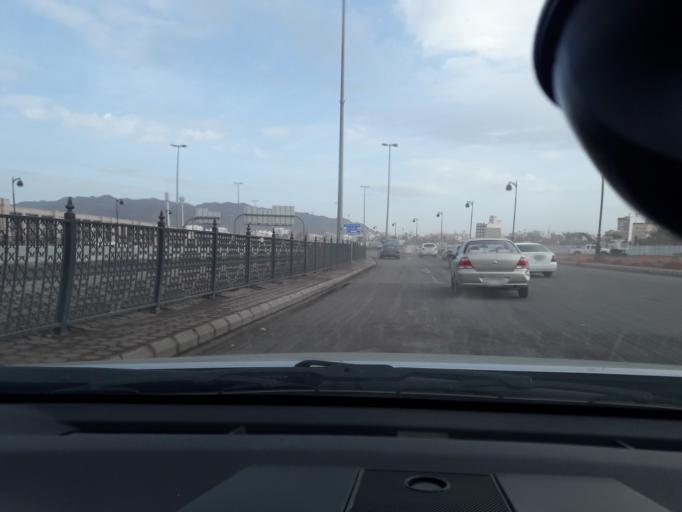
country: SA
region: Al Madinah al Munawwarah
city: Medina
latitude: 24.4650
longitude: 39.6177
